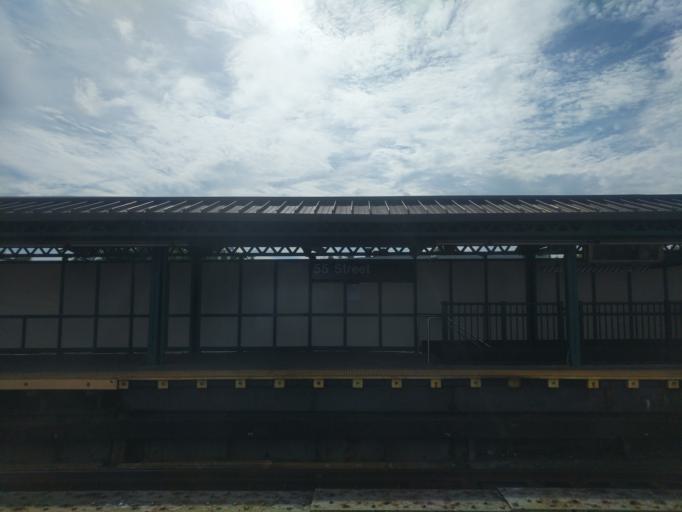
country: US
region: New York
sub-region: Kings County
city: Bensonhurst
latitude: 40.6313
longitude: -73.9956
